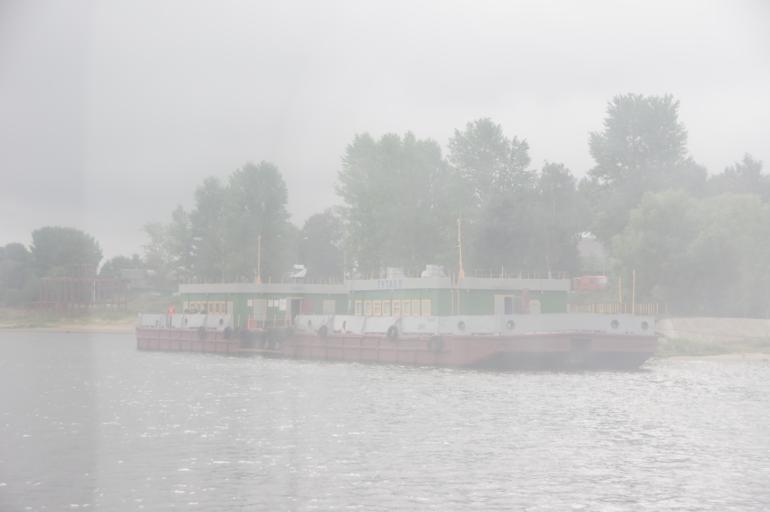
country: RU
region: Jaroslavl
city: Tutayev
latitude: 57.8782
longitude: 39.5315
